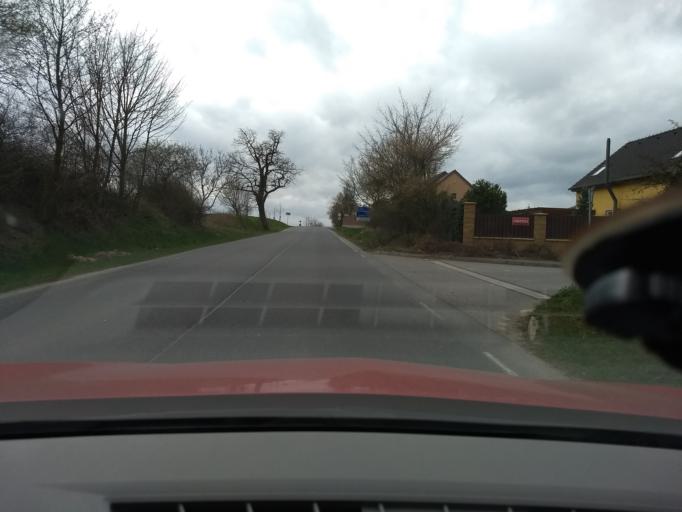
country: CZ
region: Central Bohemia
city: Unhost'
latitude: 50.0816
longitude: 14.1398
